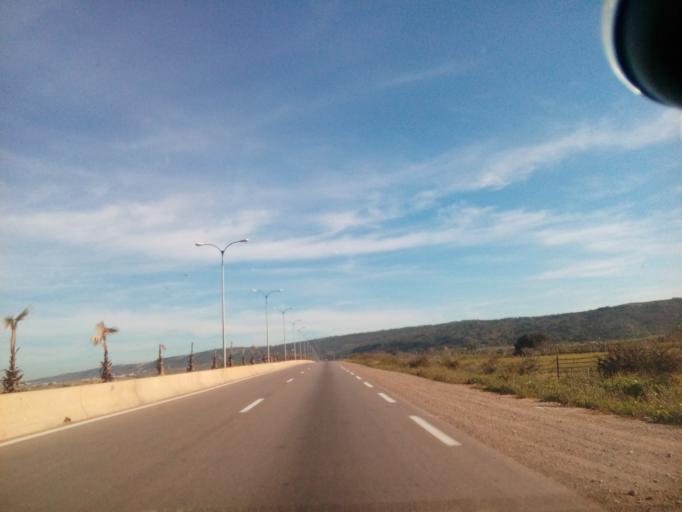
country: DZ
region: Mostaganem
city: Mostaganem
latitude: 35.8382
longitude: 0.0013
